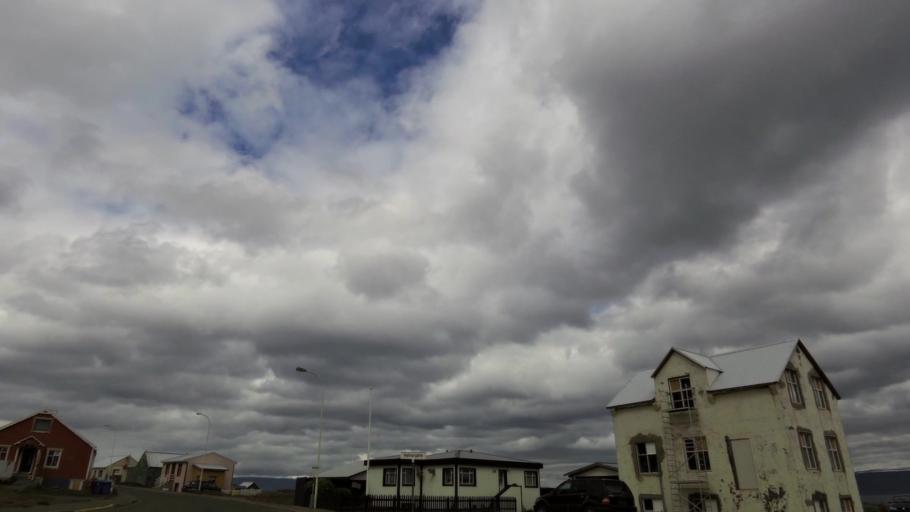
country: IS
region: Westfjords
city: Isafjoerdur
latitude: 66.1601
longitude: -23.2476
